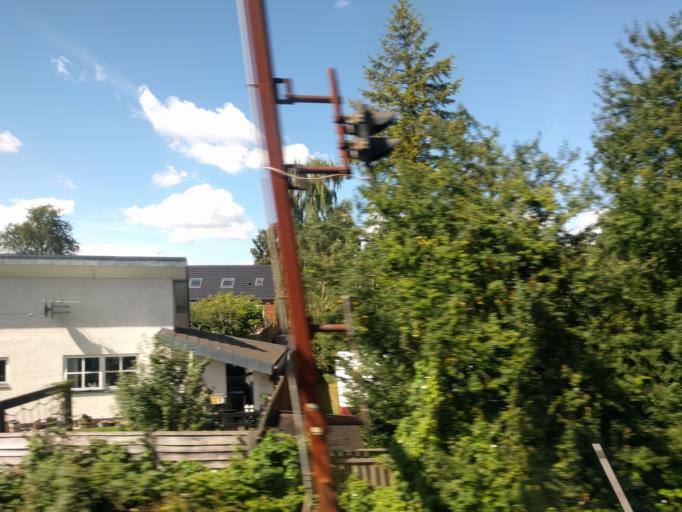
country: DK
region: Zealand
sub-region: Roskilde Kommune
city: Roskilde
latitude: 55.6303
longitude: 12.0710
